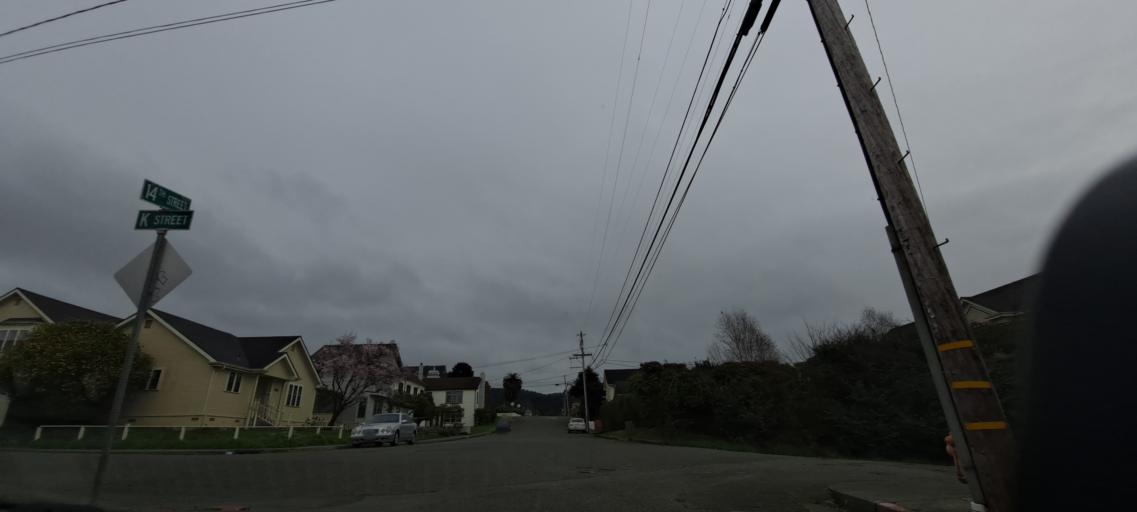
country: US
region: California
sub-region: Humboldt County
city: Arcata
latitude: 40.8737
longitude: -124.0886
